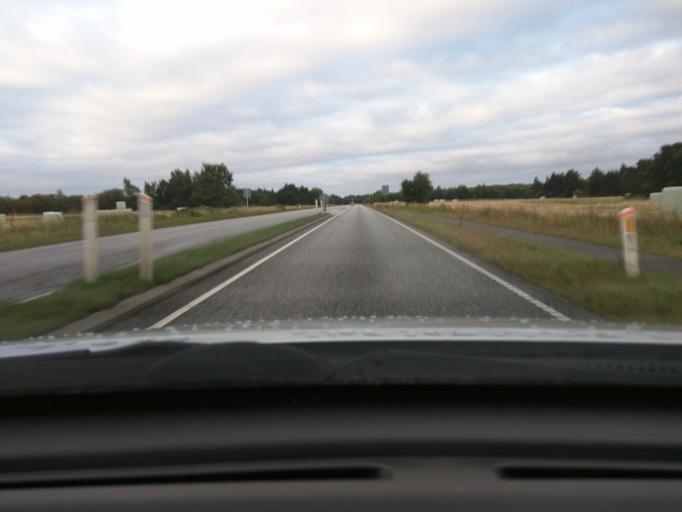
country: DK
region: Central Jutland
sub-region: Viborg Kommune
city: Viborg
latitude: 56.4124
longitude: 9.3762
